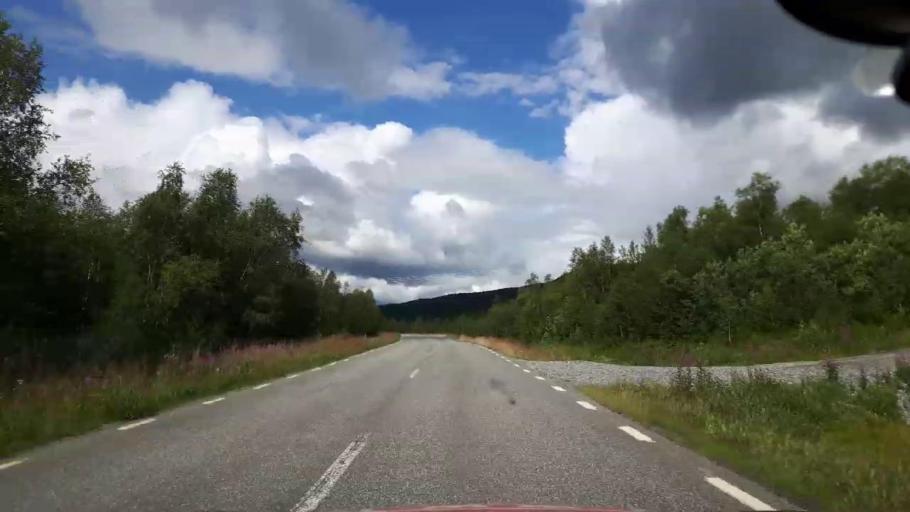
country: NO
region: Nordland
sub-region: Hattfjelldal
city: Hattfjelldal
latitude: 65.0599
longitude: 14.7140
